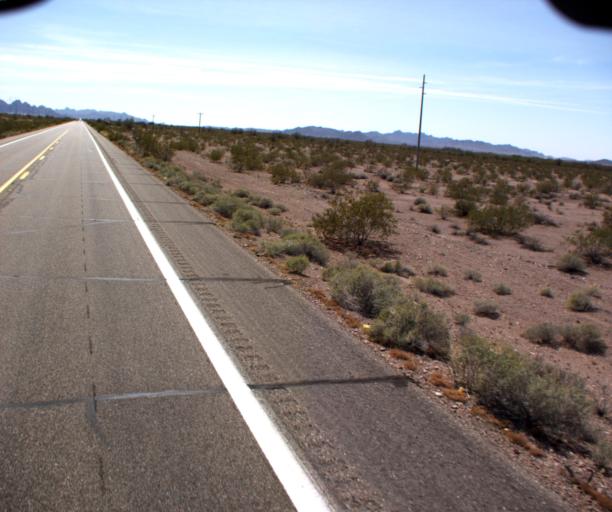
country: US
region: Arizona
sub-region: La Paz County
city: Quartzsite
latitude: 33.4095
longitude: -114.2172
